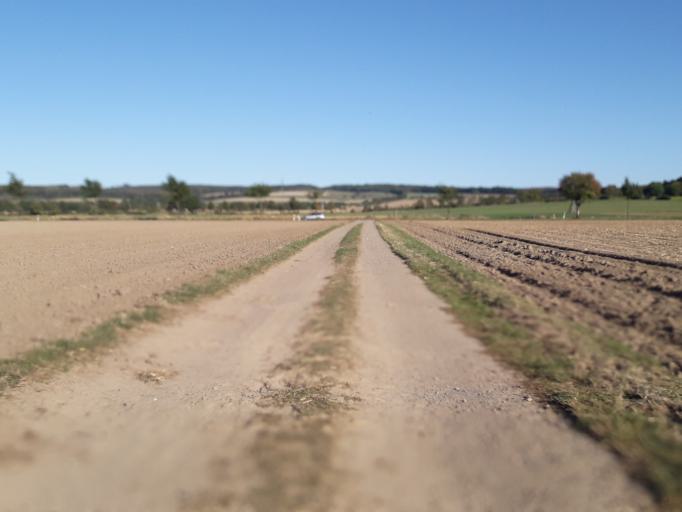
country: DE
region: North Rhine-Westphalia
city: Bad Lippspringe
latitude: 51.7621
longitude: 8.8327
